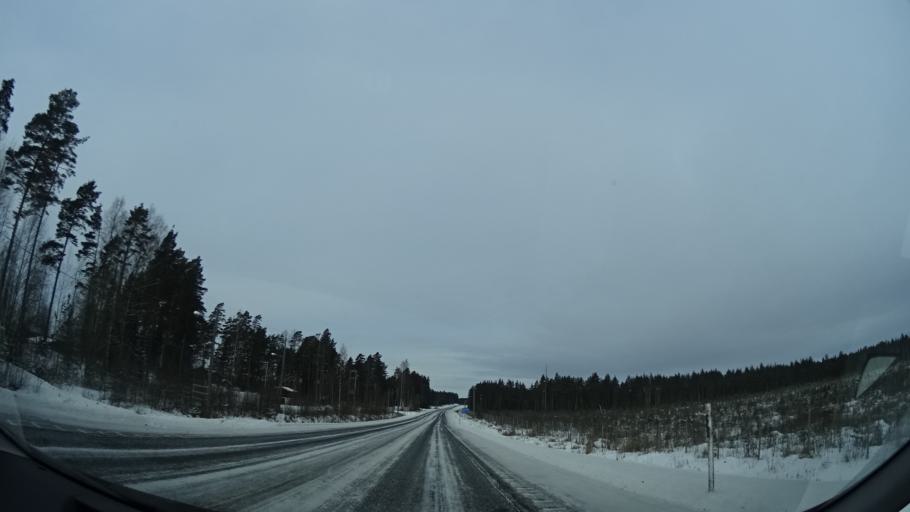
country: FI
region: Uusimaa
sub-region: Helsinki
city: Kaerkoelae
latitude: 60.6389
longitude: 23.8919
